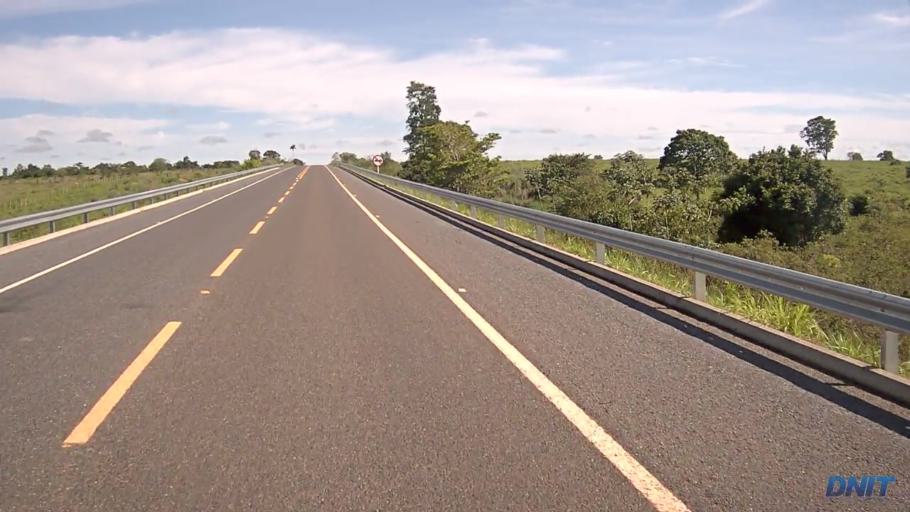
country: BR
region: Goias
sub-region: Sao Miguel Do Araguaia
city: Sao Miguel do Araguaia
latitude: -13.4507
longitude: -50.1206
